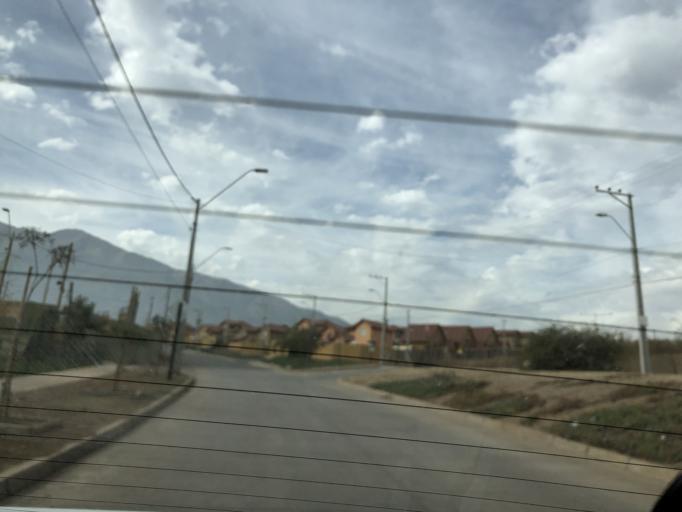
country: CL
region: Santiago Metropolitan
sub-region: Provincia de Cordillera
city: Puente Alto
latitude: -33.5870
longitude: -70.5333
